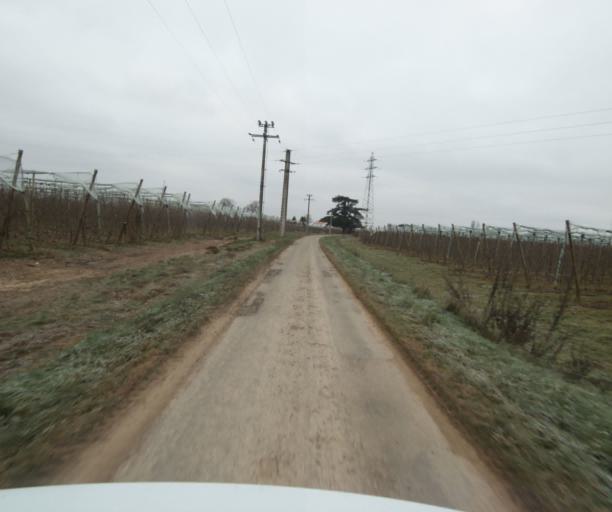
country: FR
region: Midi-Pyrenees
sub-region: Departement du Tarn-et-Garonne
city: Moissac
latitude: 44.1059
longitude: 1.1471
